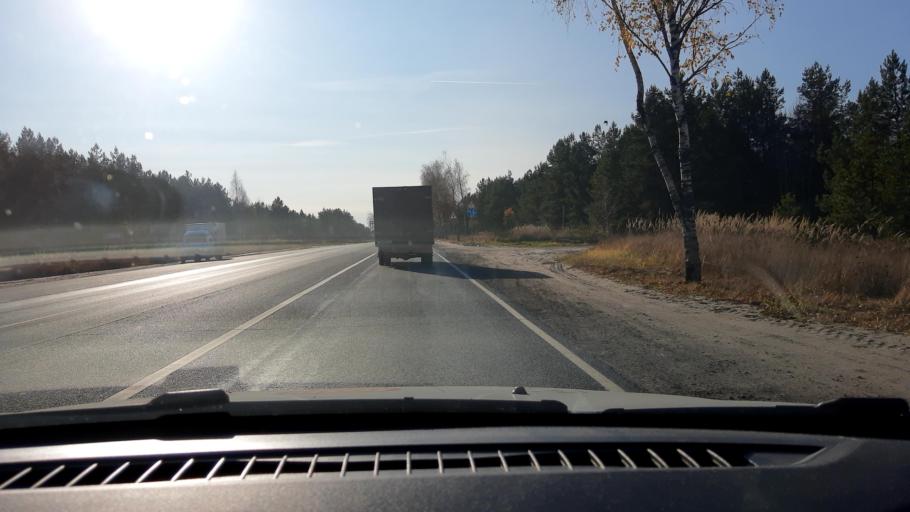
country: RU
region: Nizjnij Novgorod
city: Dzerzhinsk
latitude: 56.2909
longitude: 43.4759
